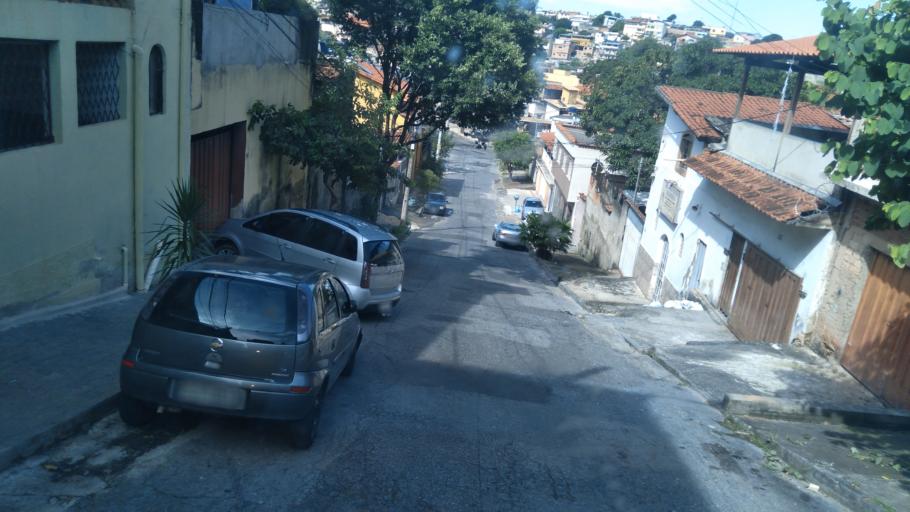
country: BR
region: Minas Gerais
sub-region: Belo Horizonte
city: Belo Horizonte
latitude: -19.8641
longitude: -43.9023
